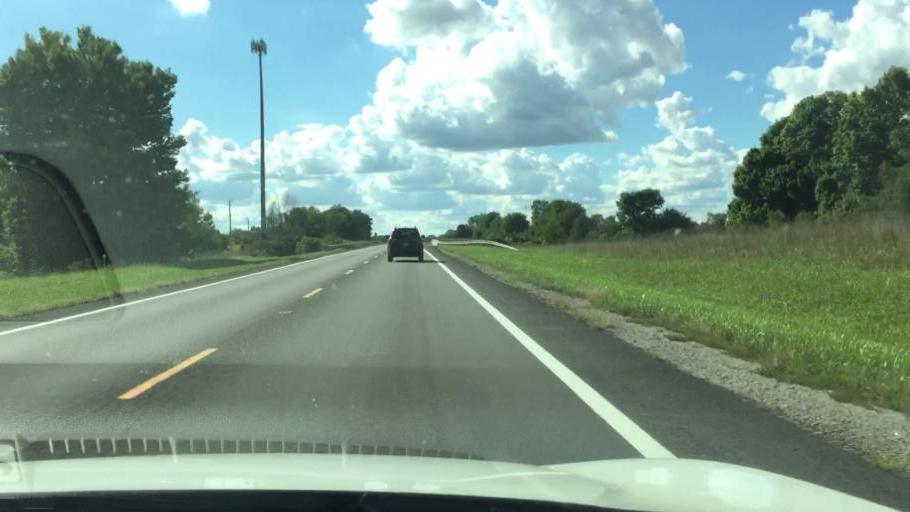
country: US
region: Ohio
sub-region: Clark County
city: Northridge
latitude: 39.9769
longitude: -83.7537
